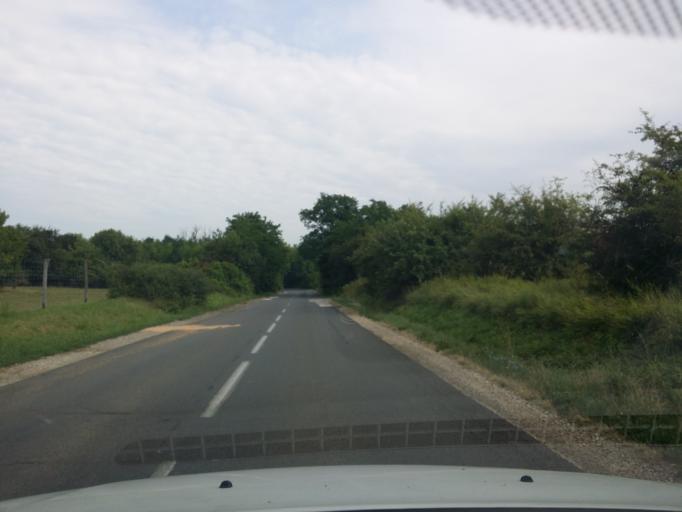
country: HU
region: Pest
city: Acsa
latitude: 47.8081
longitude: 19.3877
